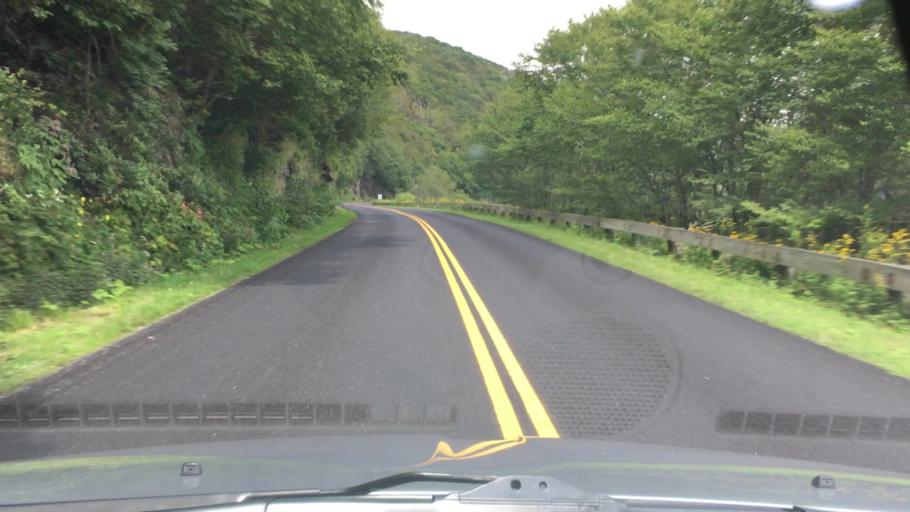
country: US
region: North Carolina
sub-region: Buncombe County
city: Swannanoa
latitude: 35.6932
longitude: -82.3829
